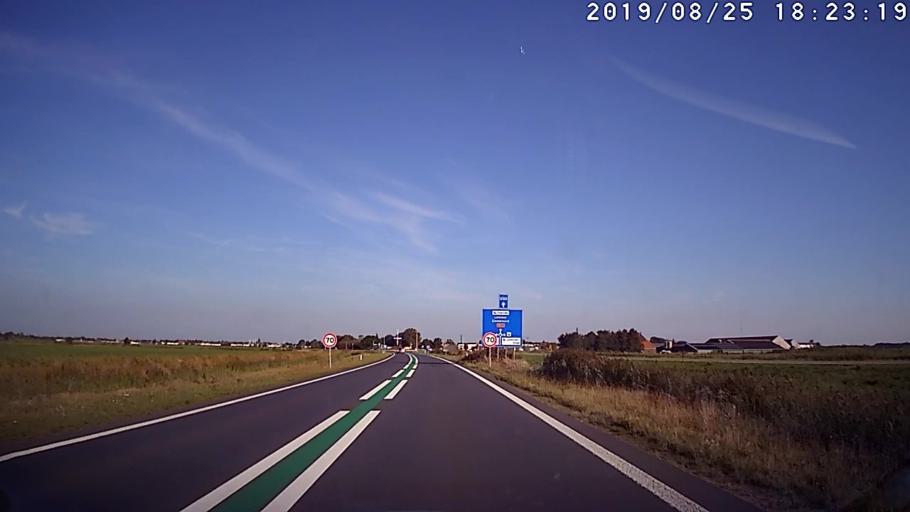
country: NL
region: Friesland
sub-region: Gemeente Lemsterland
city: Lemmer
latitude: 52.8571
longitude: 5.6628
